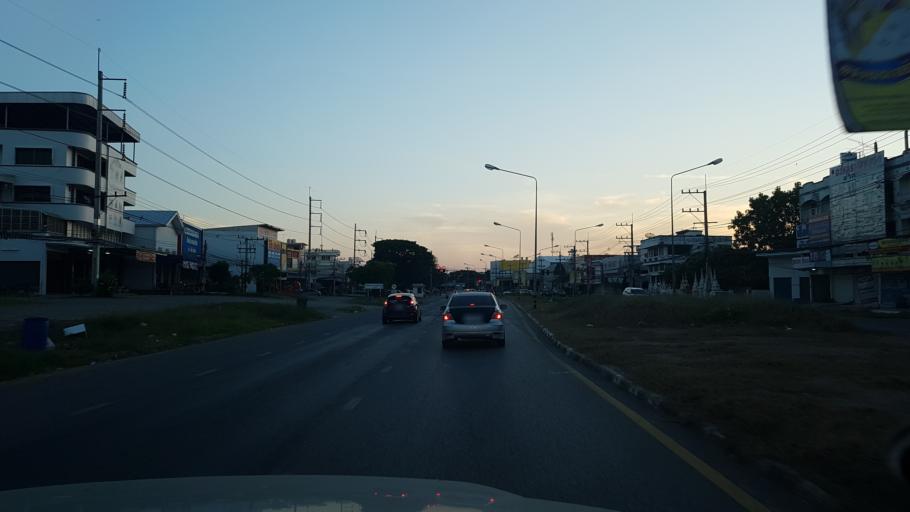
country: TH
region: Khon Kaen
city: Chum Phae
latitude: 16.5382
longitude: 102.1071
